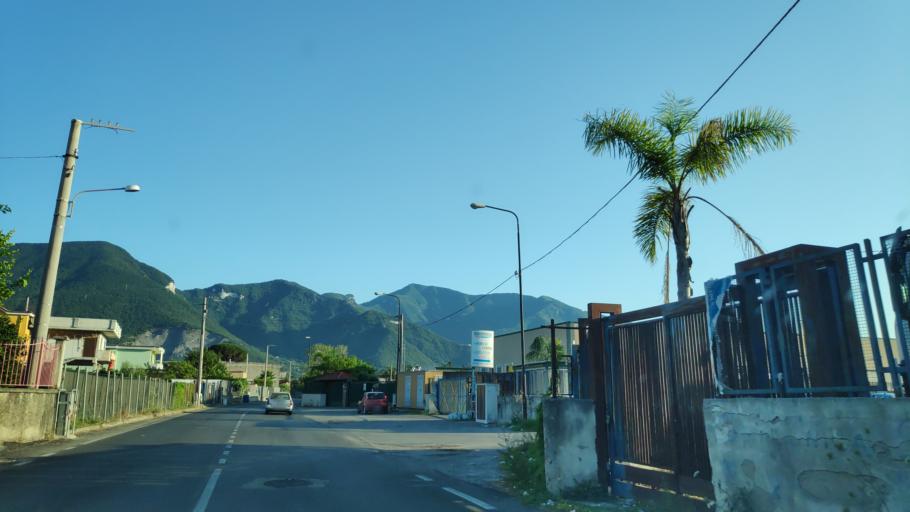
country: IT
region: Campania
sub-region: Provincia di Salerno
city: Pagani
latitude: 40.7592
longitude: 14.6156
